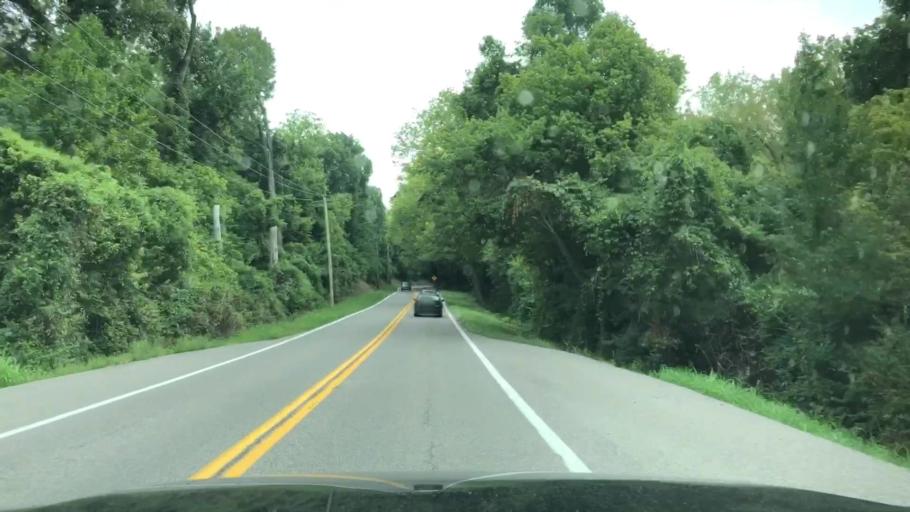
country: US
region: Missouri
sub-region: Saint Louis County
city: Hazelwood
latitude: 38.8109
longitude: -90.3899
